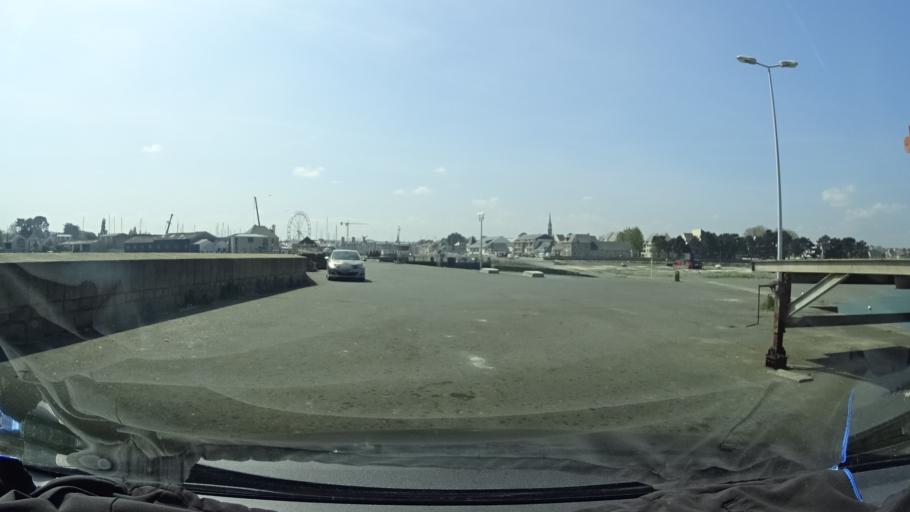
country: FR
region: Brittany
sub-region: Departement des Cotes-d'Armor
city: Paimpol
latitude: 48.7849
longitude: -3.0408
